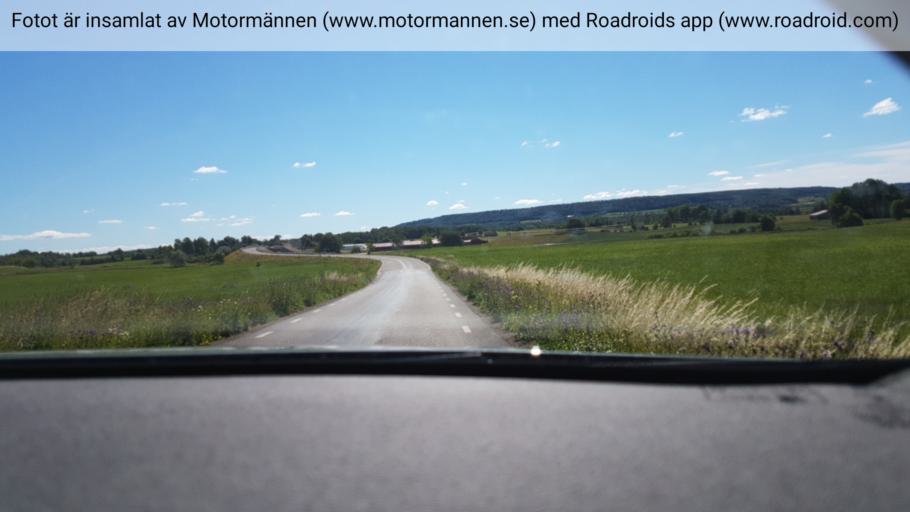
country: SE
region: Vaestra Goetaland
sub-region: Falkopings Kommun
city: Akarp
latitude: 58.2553
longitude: 13.6775
